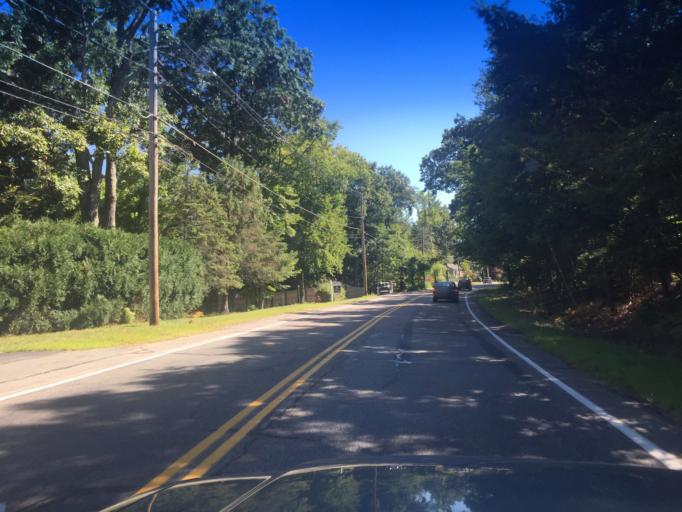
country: US
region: Massachusetts
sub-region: Norfolk County
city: Sharon
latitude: 42.1435
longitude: -71.2058
